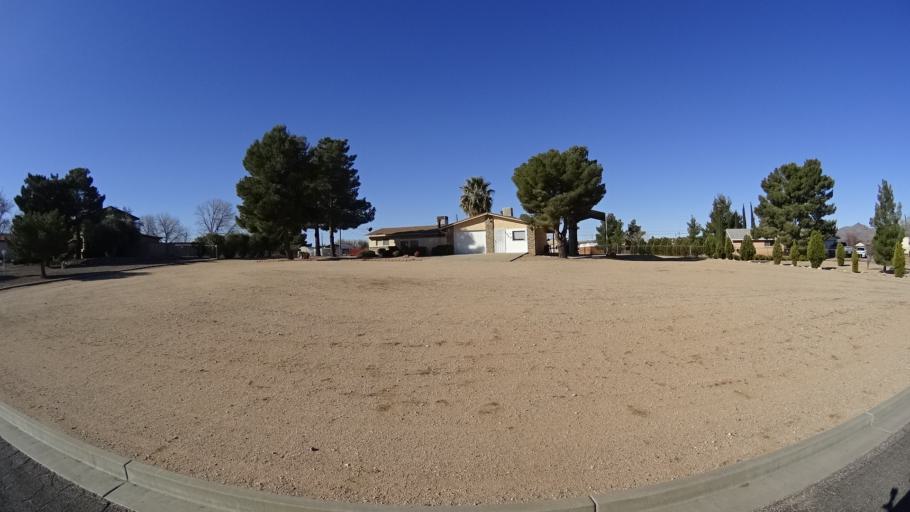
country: US
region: Arizona
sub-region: Mohave County
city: Kingman
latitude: 35.2023
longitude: -114.0039
